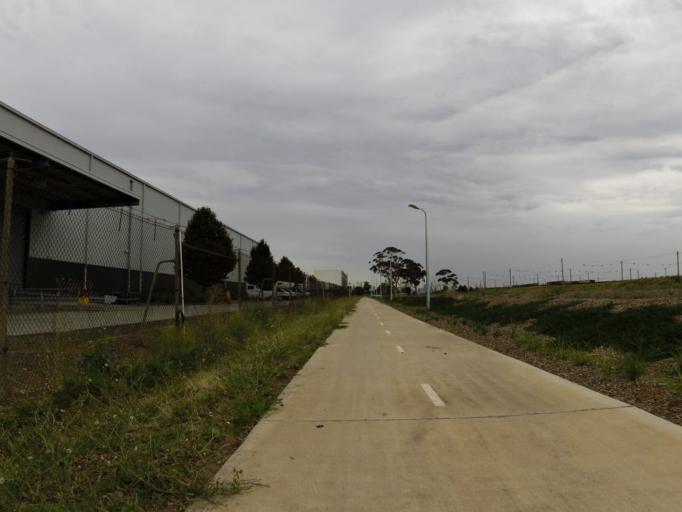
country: AU
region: Victoria
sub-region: Maribyrnong
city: Braybrook
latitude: -37.7972
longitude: 144.8587
